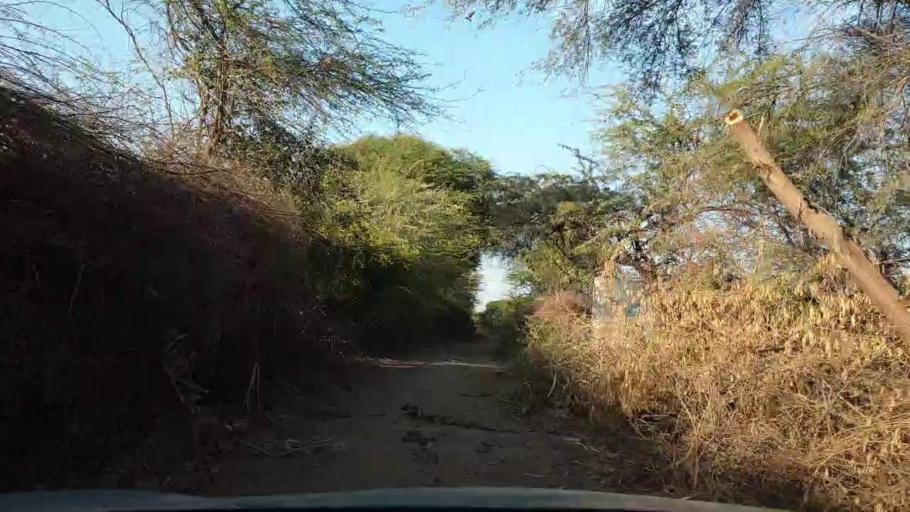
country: PK
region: Sindh
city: Tando Adam
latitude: 25.7012
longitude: 68.6923
